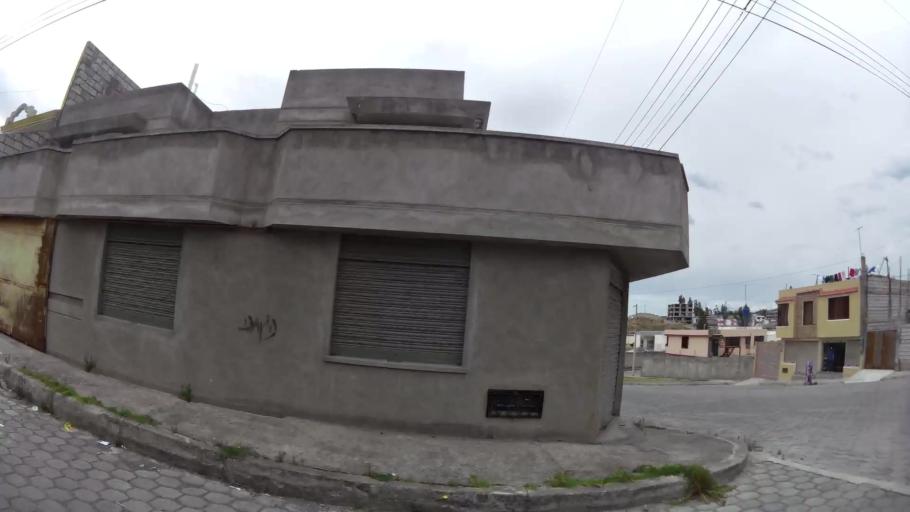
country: EC
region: Cotopaxi
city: Latacunga
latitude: -0.9523
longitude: -78.6042
